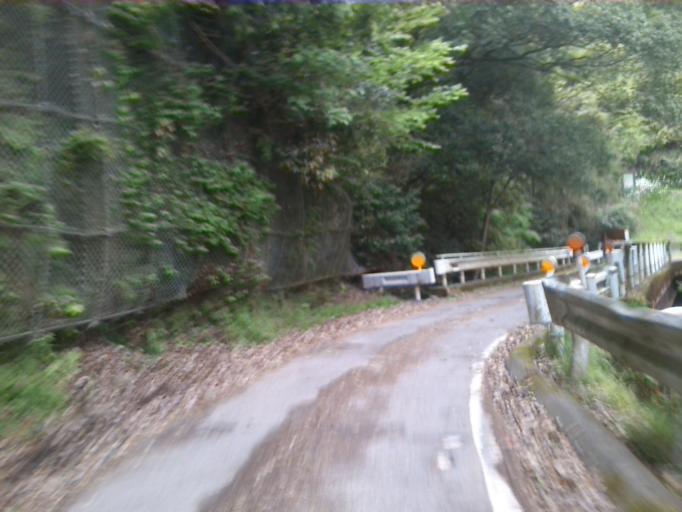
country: JP
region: Kyoto
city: Muko
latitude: 34.9531
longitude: 135.6418
